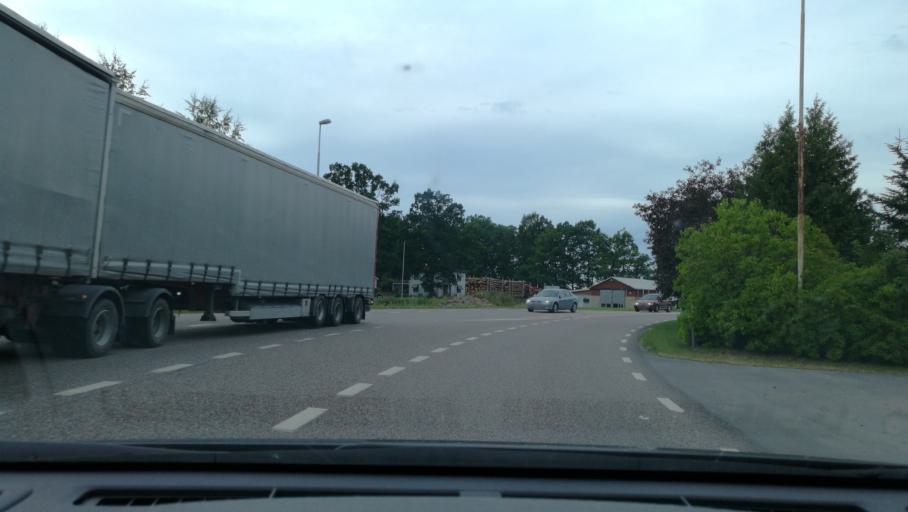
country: SE
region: Soedermanland
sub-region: Katrineholms Kommun
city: Katrineholm
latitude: 59.1520
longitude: 16.1088
